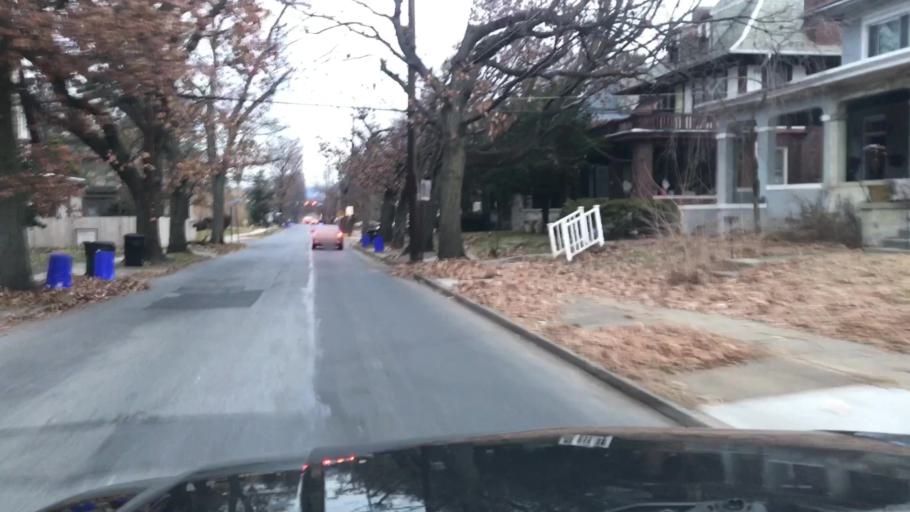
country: US
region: Pennsylvania
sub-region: Dauphin County
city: Harrisburg
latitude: 40.2736
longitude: -76.8677
